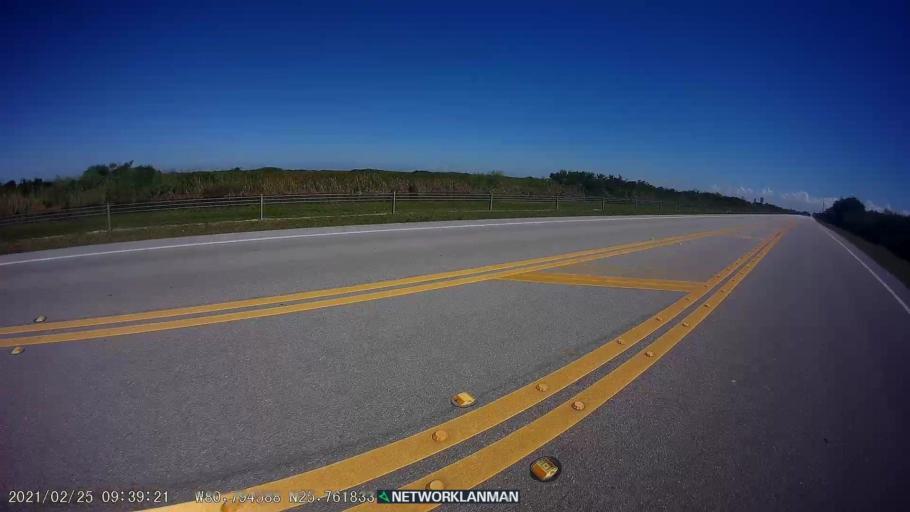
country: US
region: Florida
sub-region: Miami-Dade County
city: Kendall West
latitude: 25.7616
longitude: -80.7944
